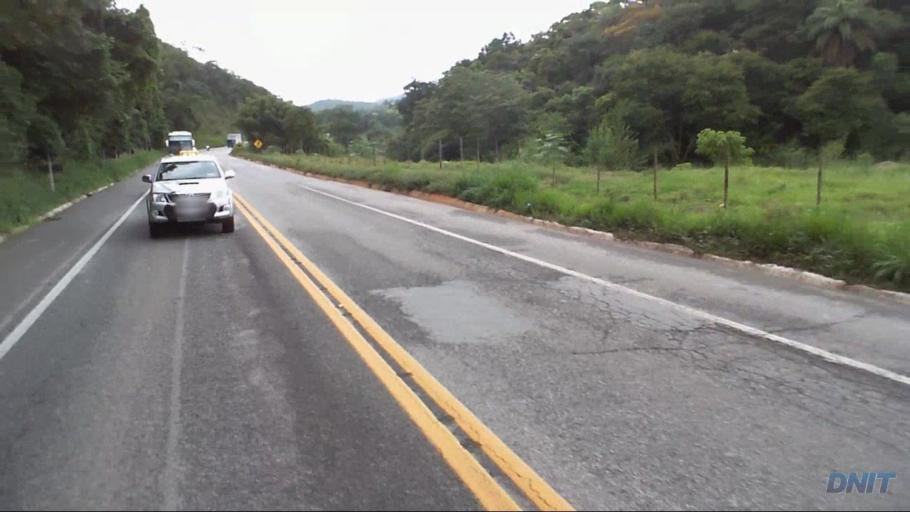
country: BR
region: Minas Gerais
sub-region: Joao Monlevade
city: Joao Monlevade
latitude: -19.8365
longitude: -43.3456
